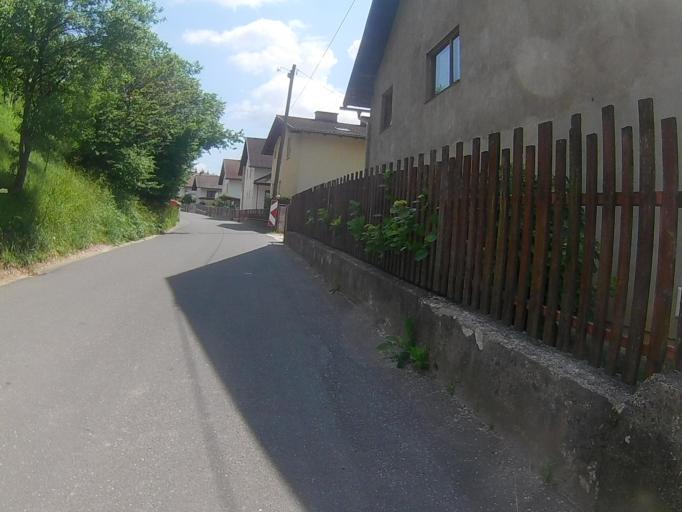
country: SI
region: Maribor
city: Kamnica
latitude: 46.5738
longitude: 15.6093
